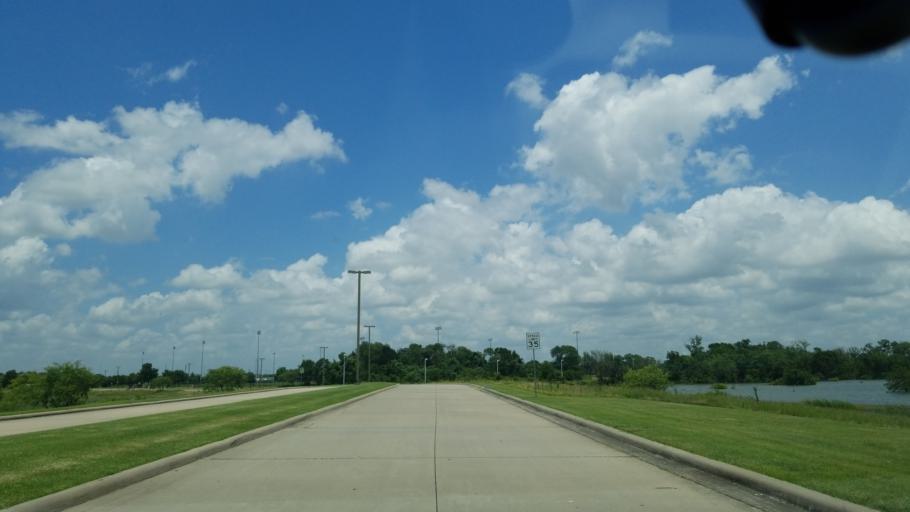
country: US
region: Texas
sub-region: Dallas County
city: Carrollton
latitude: 32.9617
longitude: -96.9418
